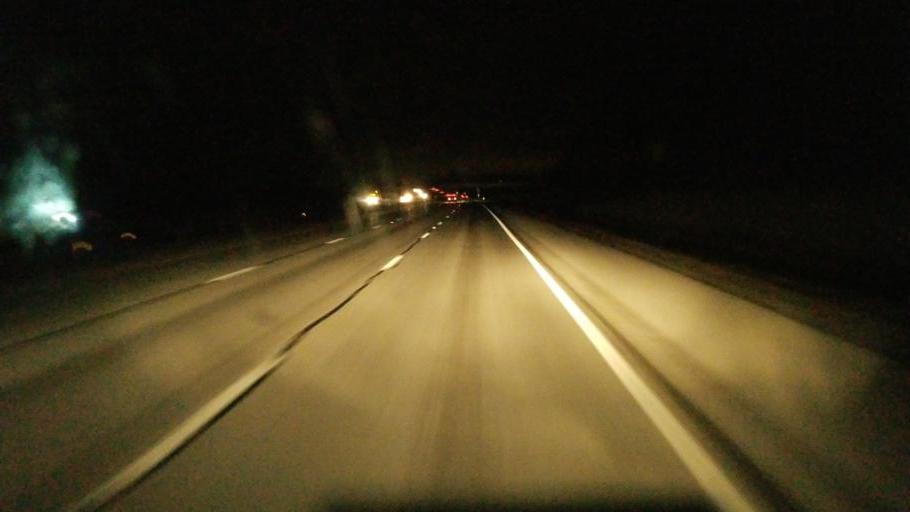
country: US
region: Ohio
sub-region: Madison County
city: Choctaw Lake
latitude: 39.9385
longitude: -83.5660
